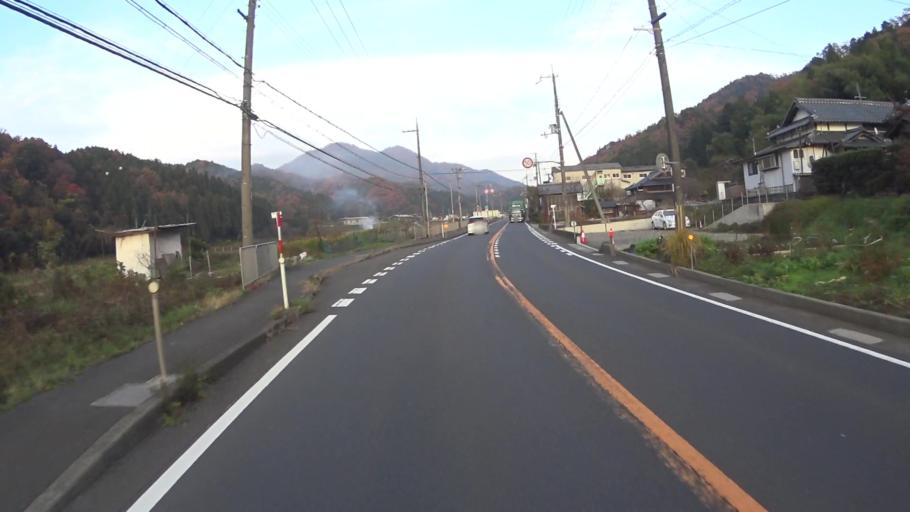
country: JP
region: Kyoto
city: Maizuru
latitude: 35.4824
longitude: 135.4443
